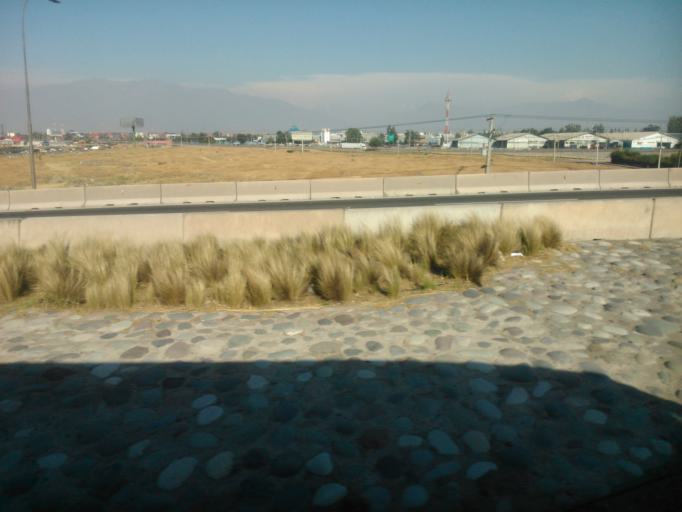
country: CL
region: Santiago Metropolitan
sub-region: Provincia de Maipo
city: San Bernardo
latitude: -33.5527
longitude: -70.7094
